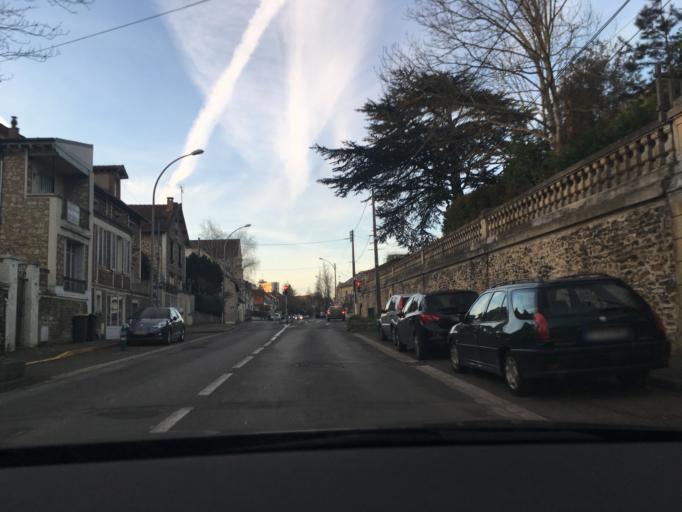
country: FR
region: Ile-de-France
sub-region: Departement de Seine-et-Marne
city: Melun
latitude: 48.5408
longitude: 2.6517
